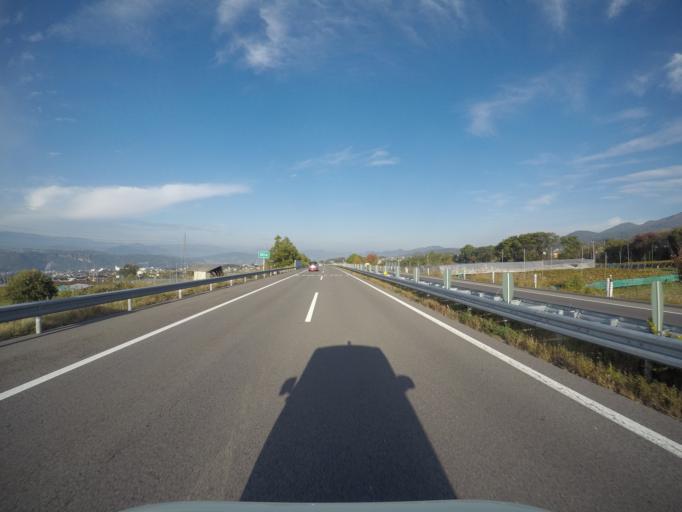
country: JP
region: Nagano
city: Komoro
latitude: 36.3533
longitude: 138.3788
